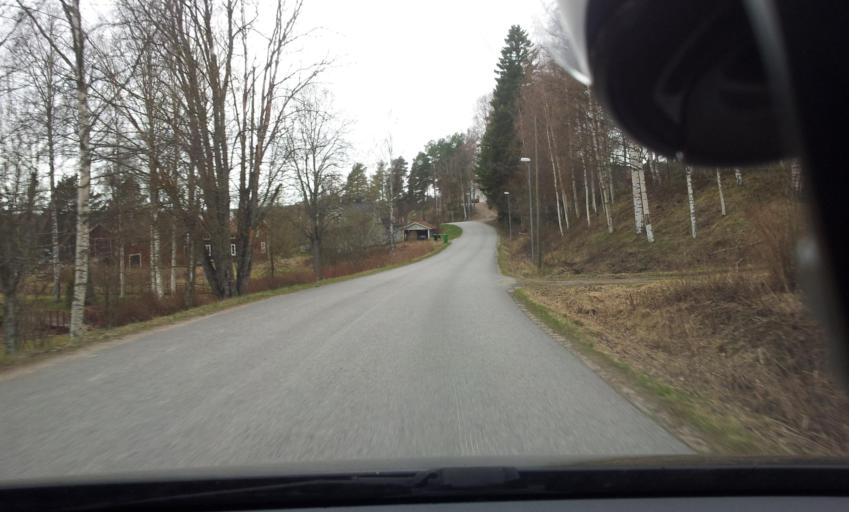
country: SE
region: Gaevleborg
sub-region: Ljusdals Kommun
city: Farila
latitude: 61.8062
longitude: 15.8555
